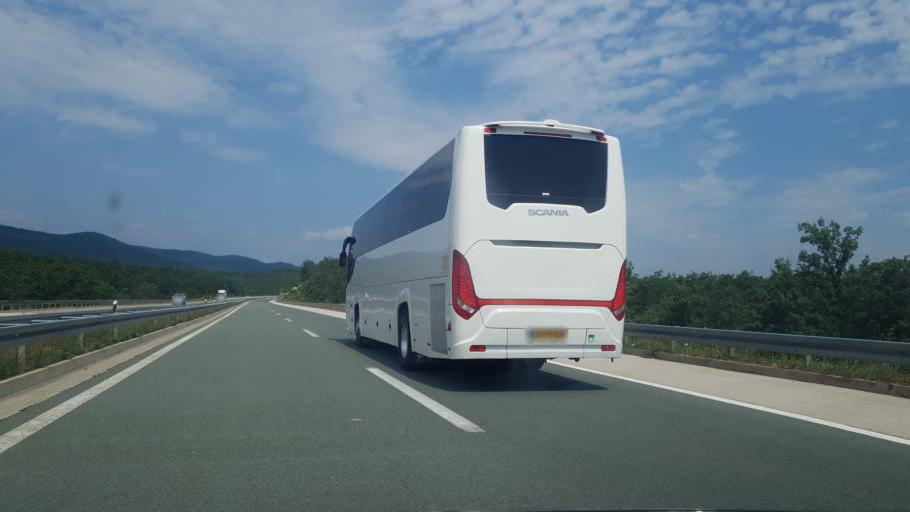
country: HR
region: Primorsko-Goranska
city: Matulji
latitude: 45.4320
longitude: 14.2862
